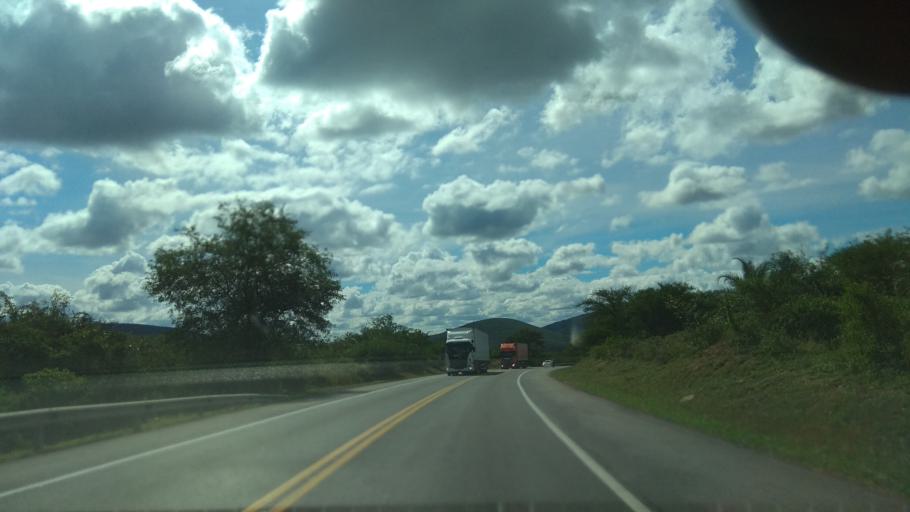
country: BR
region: Bahia
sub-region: Santa Ines
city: Santa Ines
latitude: -13.3066
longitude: -40.0263
